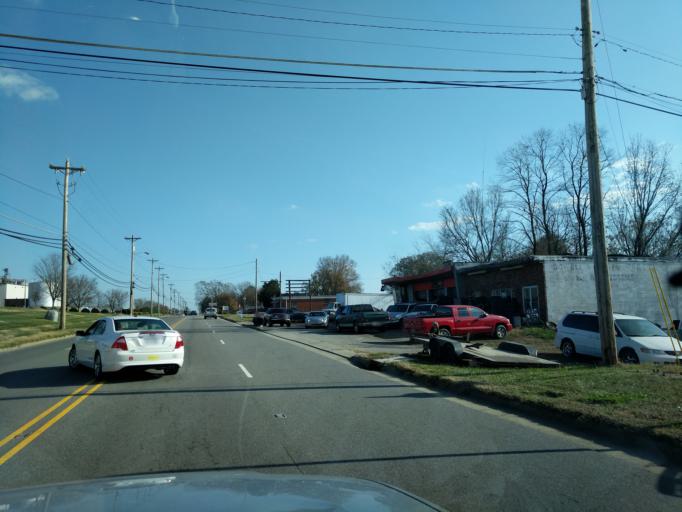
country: US
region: North Carolina
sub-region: Iredell County
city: Statesville
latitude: 35.7917
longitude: -80.9307
